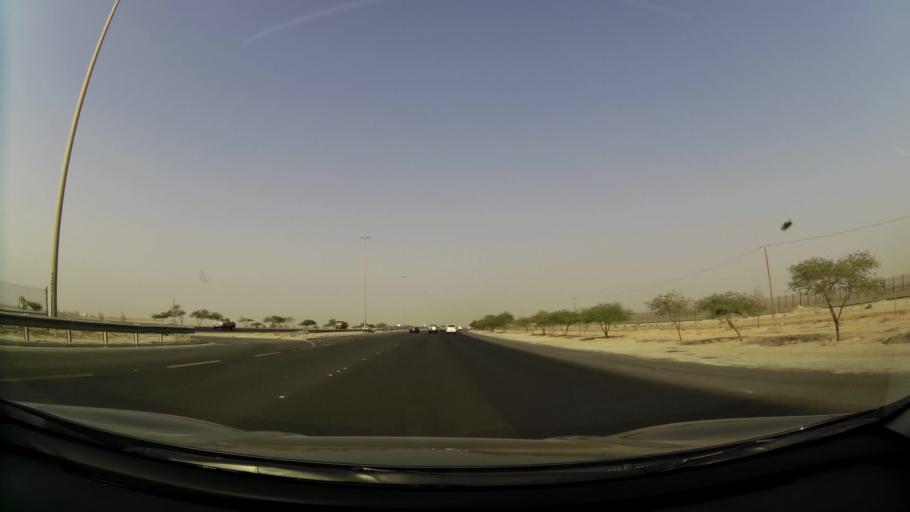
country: KW
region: Mubarak al Kabir
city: Mubarak al Kabir
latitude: 29.1744
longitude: 48.0389
